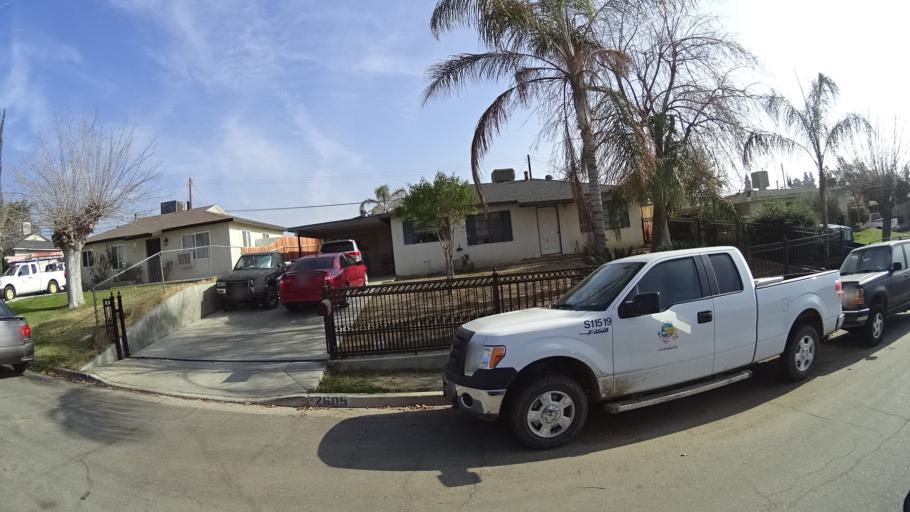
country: US
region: California
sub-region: Kern County
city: Bakersfield
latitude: 35.3916
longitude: -118.9706
